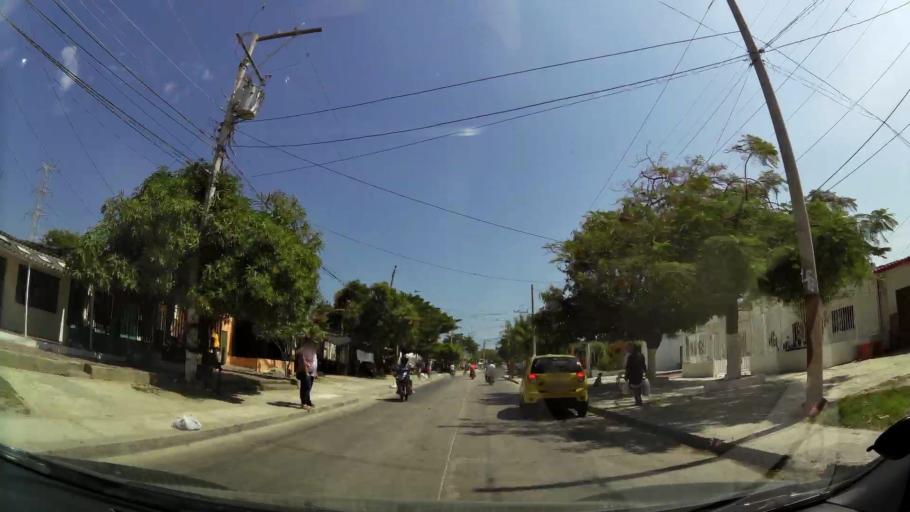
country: CO
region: Atlantico
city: Barranquilla
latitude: 10.9695
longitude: -74.8331
